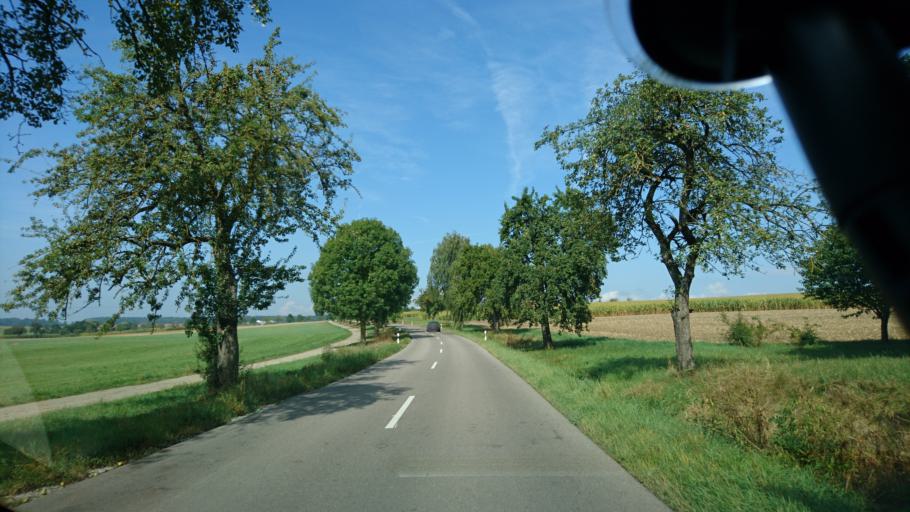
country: DE
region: Baden-Wuerttemberg
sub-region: Regierungsbezirk Stuttgart
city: Ilshofen
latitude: 49.1583
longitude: 9.9291
